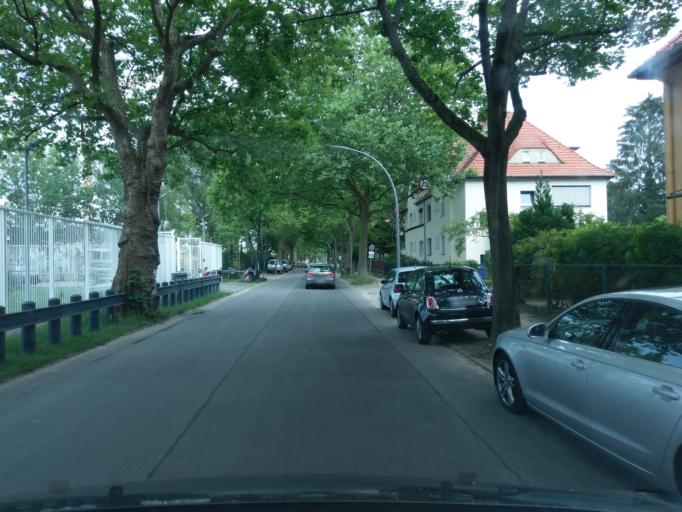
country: DE
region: Berlin
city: Dahlem
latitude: 52.4396
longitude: 13.2867
